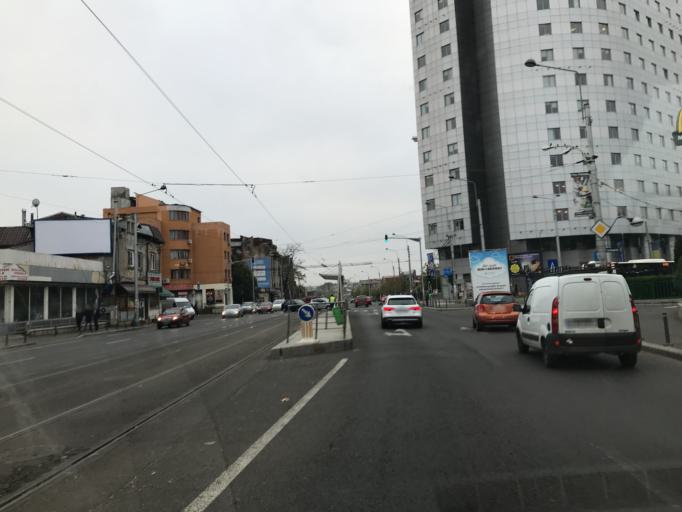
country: RO
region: Bucuresti
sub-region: Municipiul Bucuresti
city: Bucuresti
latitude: 44.4487
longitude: 26.0827
